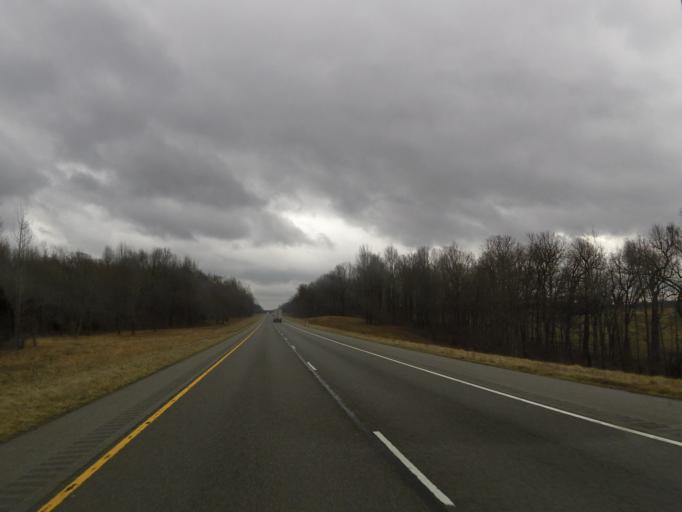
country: US
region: Illinois
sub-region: Massac County
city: Metropolis
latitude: 37.2650
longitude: -88.7358
